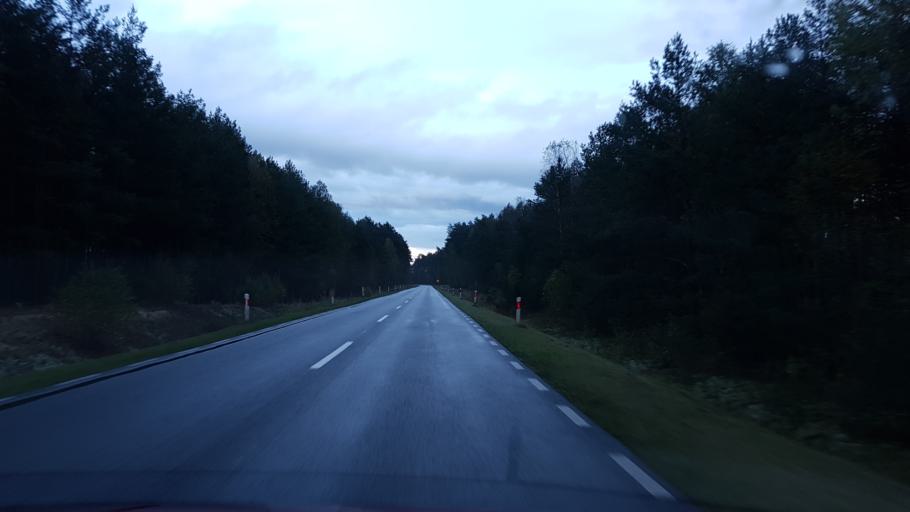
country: PL
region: Greater Poland Voivodeship
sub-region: Powiat pilski
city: Pila
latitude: 53.1911
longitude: 16.8182
